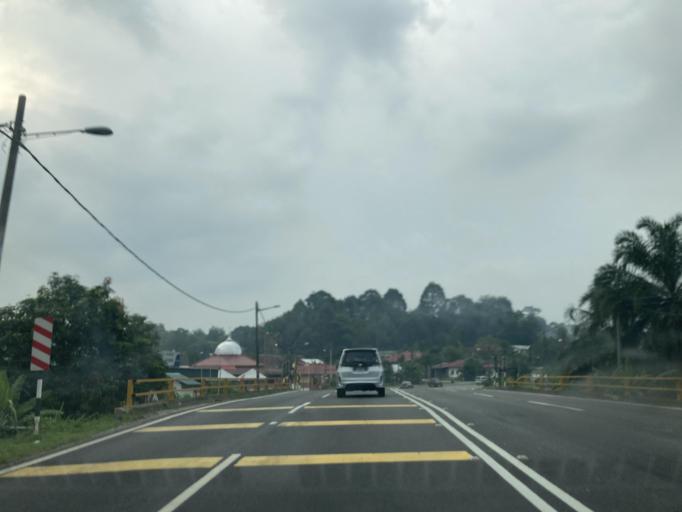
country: MY
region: Selangor
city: Kuang
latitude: 3.2104
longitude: 101.5357
